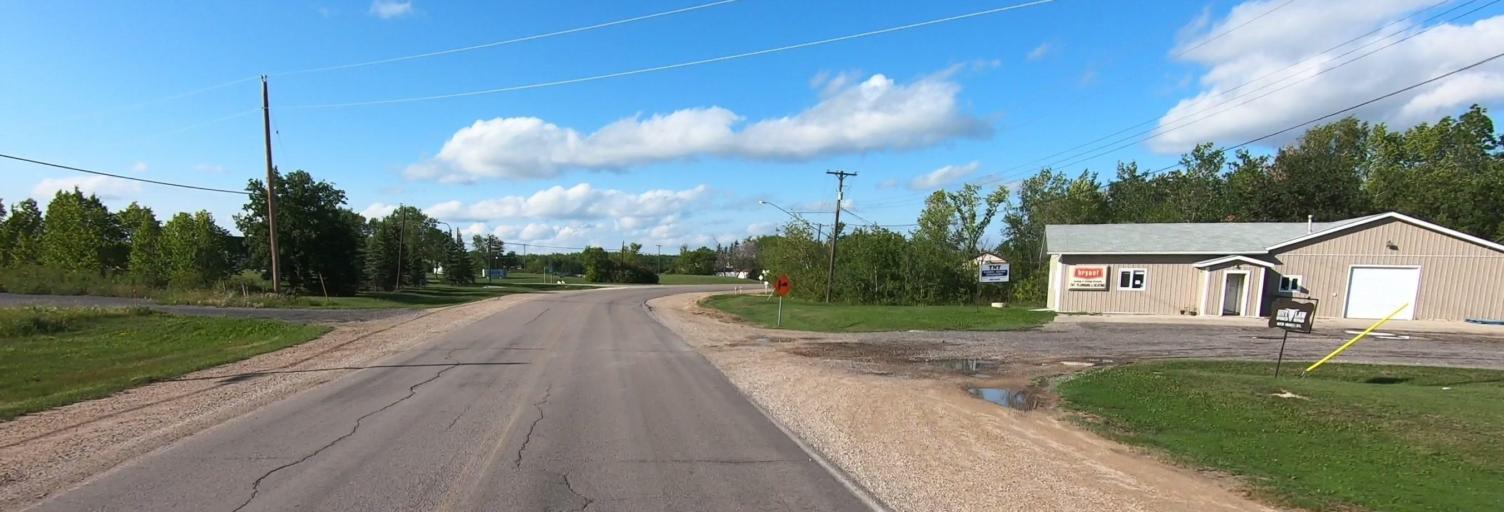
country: CA
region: Manitoba
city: Selkirk
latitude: 50.1653
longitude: -96.8674
